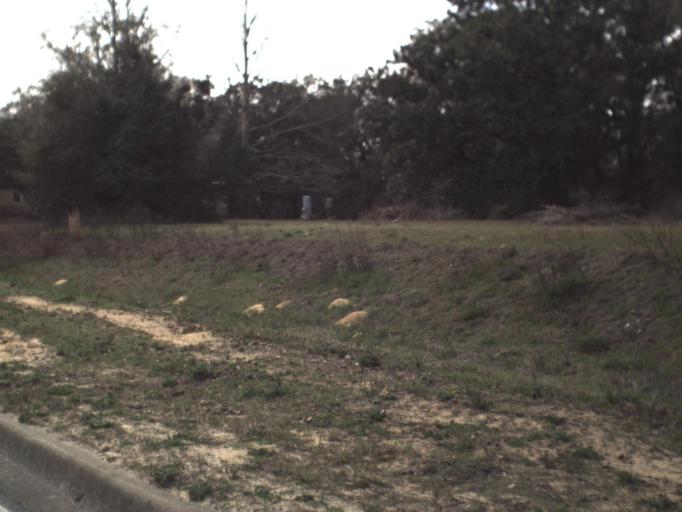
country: US
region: Florida
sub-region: Washington County
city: Chipley
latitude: 30.6531
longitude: -85.3949
